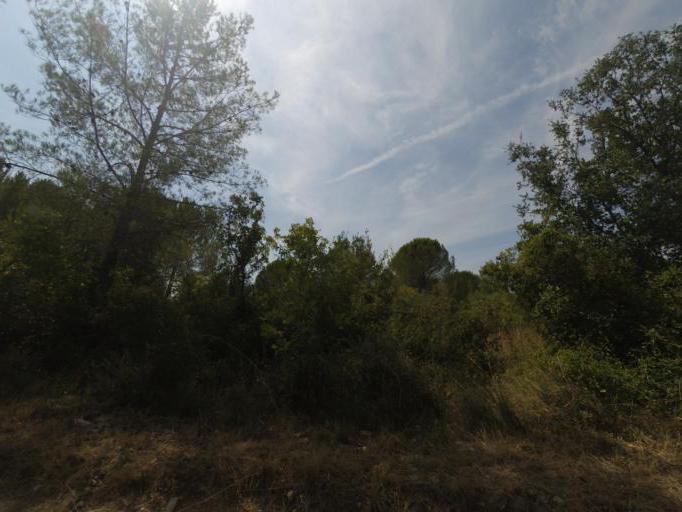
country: FR
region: Languedoc-Roussillon
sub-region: Departement du Gard
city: Aubais
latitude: 43.7681
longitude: 4.1338
